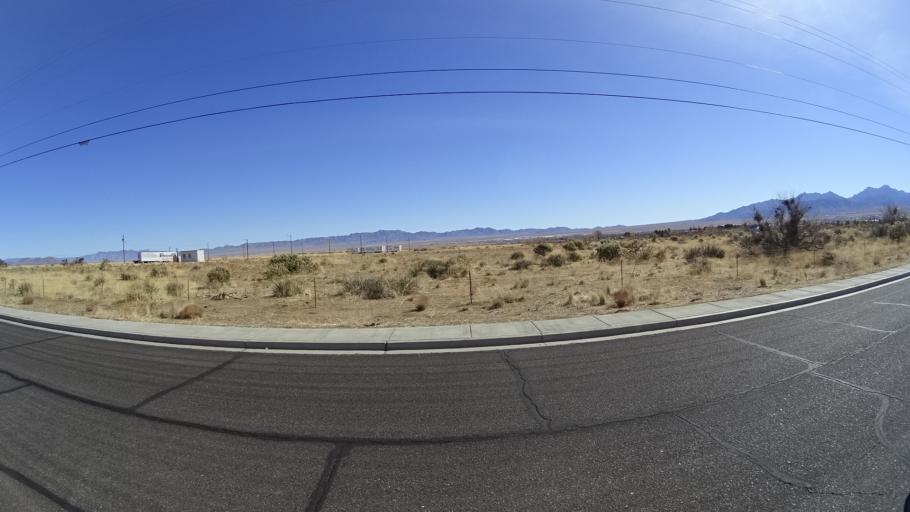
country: US
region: Arizona
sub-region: Mohave County
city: New Kingman-Butler
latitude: 35.2736
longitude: -114.0350
